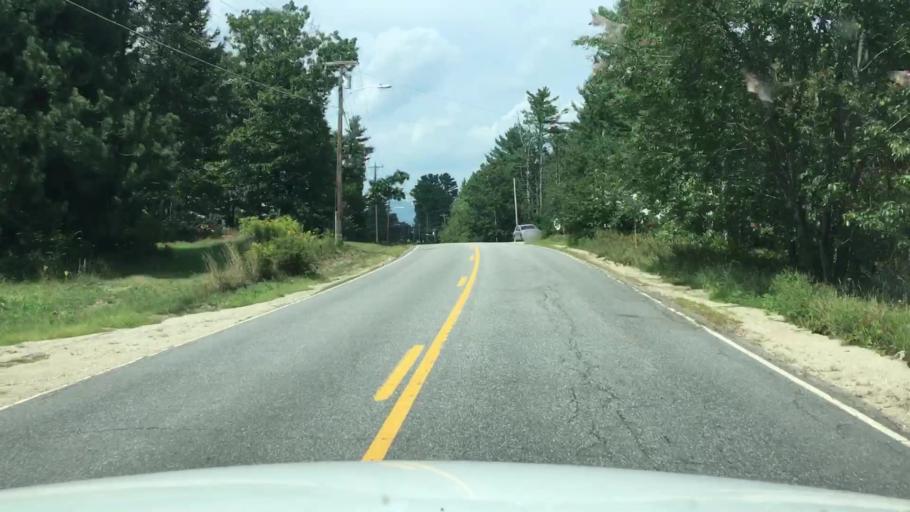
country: US
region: Maine
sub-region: Oxford County
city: Rumford
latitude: 44.6257
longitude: -70.7460
